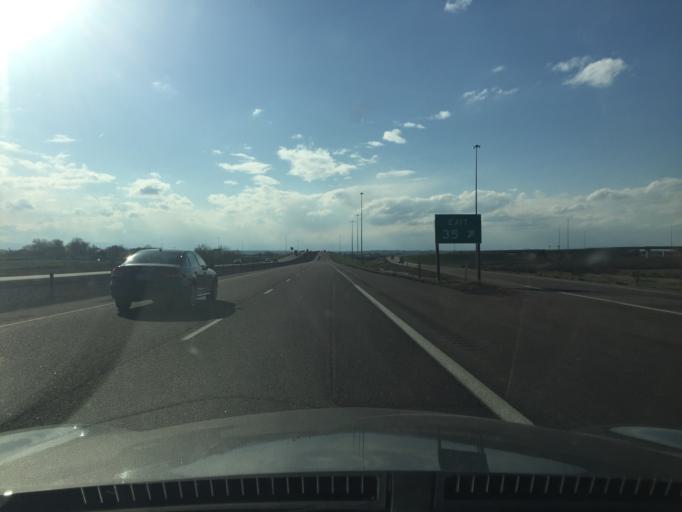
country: US
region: Colorado
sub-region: Adams County
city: Brighton
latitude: 39.9213
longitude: -104.7939
